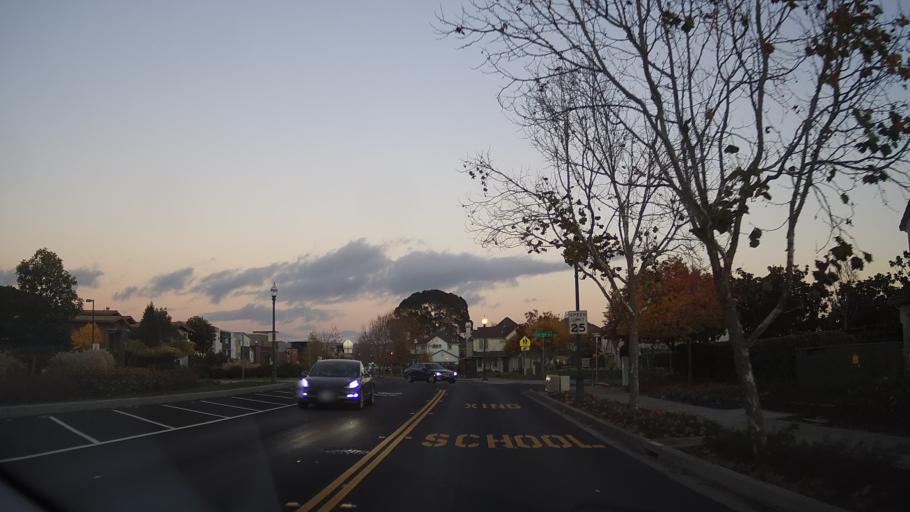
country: US
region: California
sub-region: Alameda County
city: Oakland
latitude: 37.7848
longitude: -122.2845
